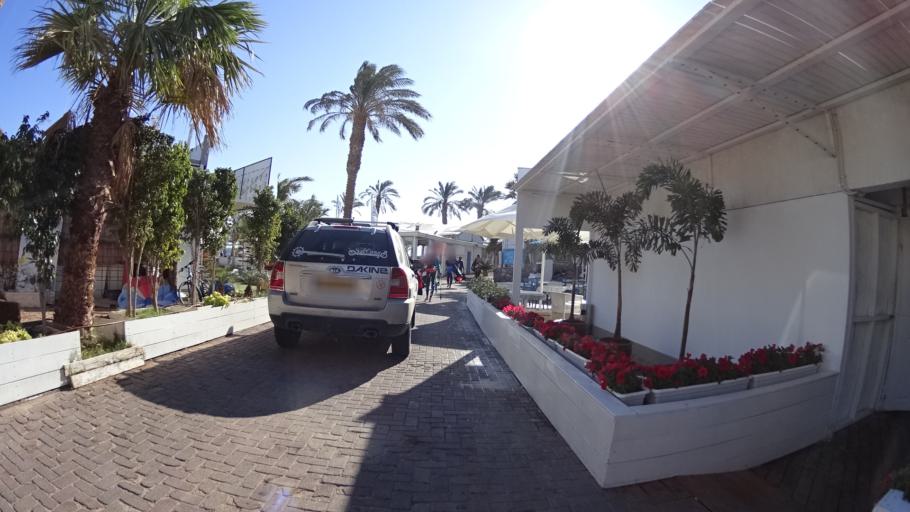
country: IL
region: Southern District
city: Eilat
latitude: 29.5138
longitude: 34.9263
